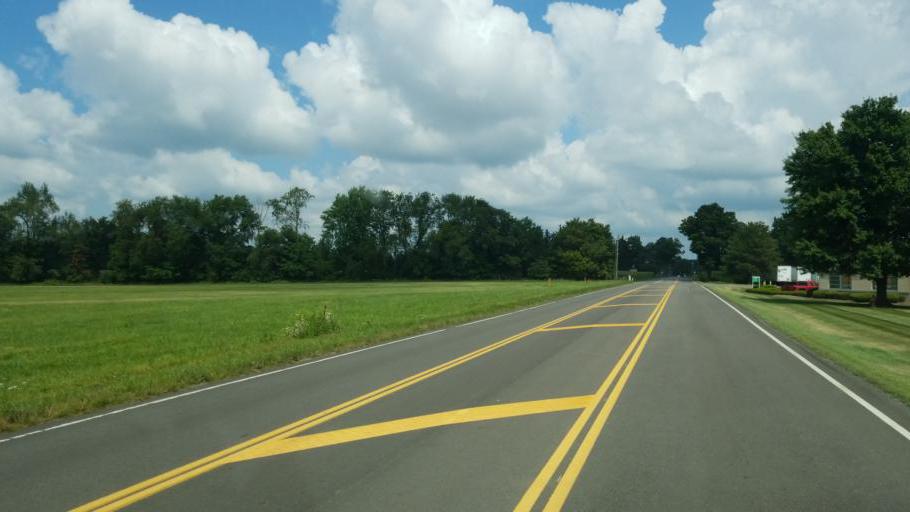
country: US
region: Ohio
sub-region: Knox County
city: Mount Vernon
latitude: 40.3660
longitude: -82.4908
